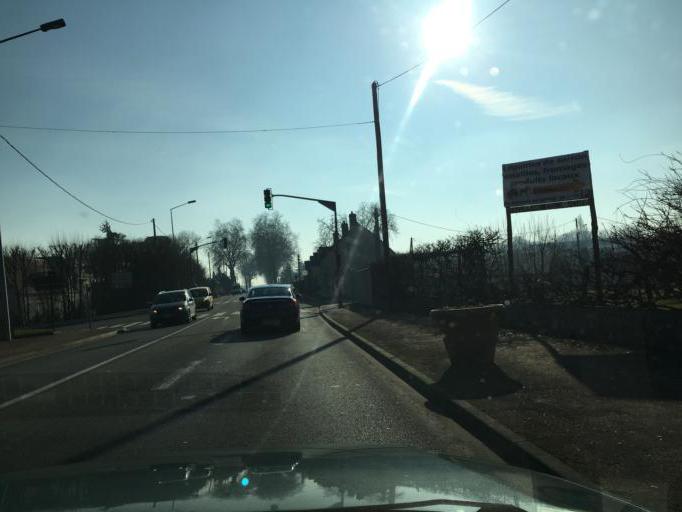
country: FR
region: Centre
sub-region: Departement du Loiret
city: Chevilly
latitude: 48.0235
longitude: 1.8747
